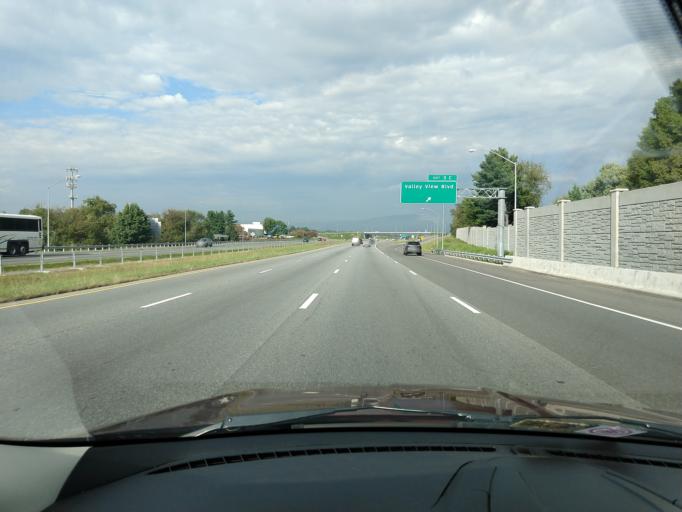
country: US
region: Virginia
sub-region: City of Roanoke
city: Roanoke
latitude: 37.2951
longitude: -79.9531
